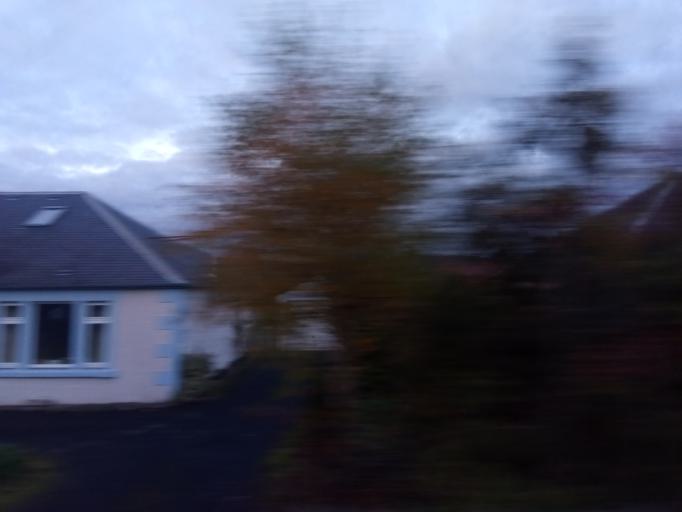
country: GB
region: Scotland
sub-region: The Scottish Borders
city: Lauder
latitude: 55.7226
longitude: -2.7556
